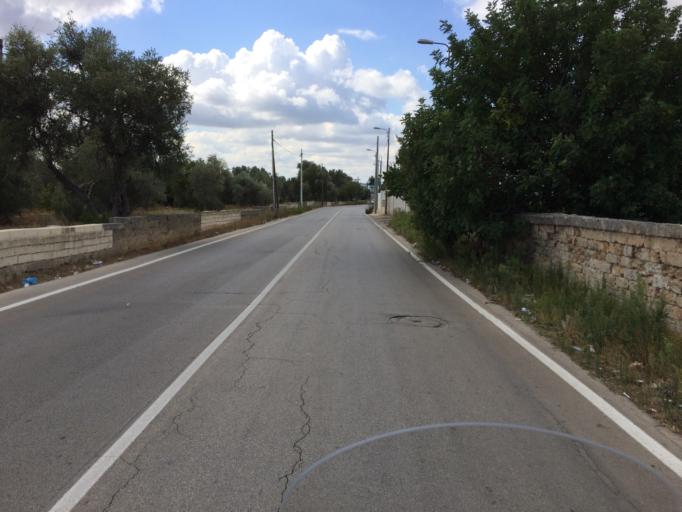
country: IT
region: Apulia
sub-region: Provincia di Bari
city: Bari
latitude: 41.1046
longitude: 16.8377
